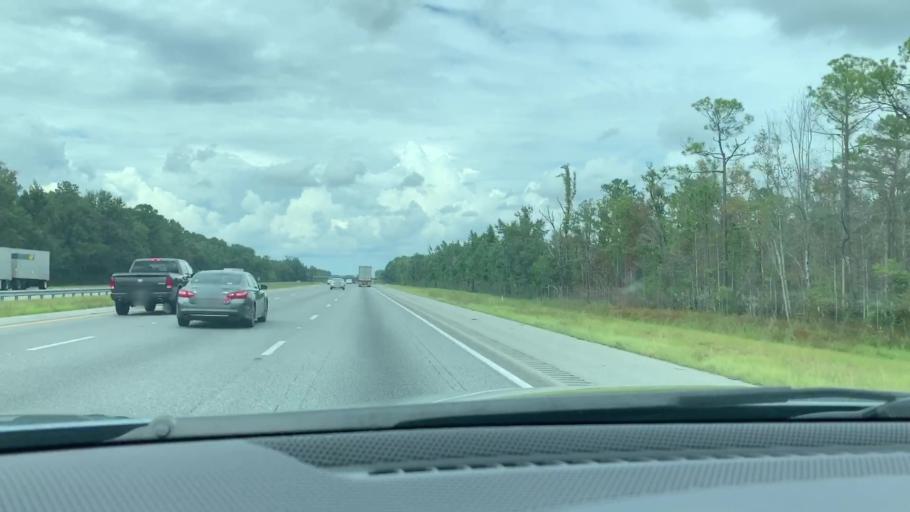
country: US
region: Georgia
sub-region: McIntosh County
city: Darien
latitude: 31.4586
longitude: -81.4459
